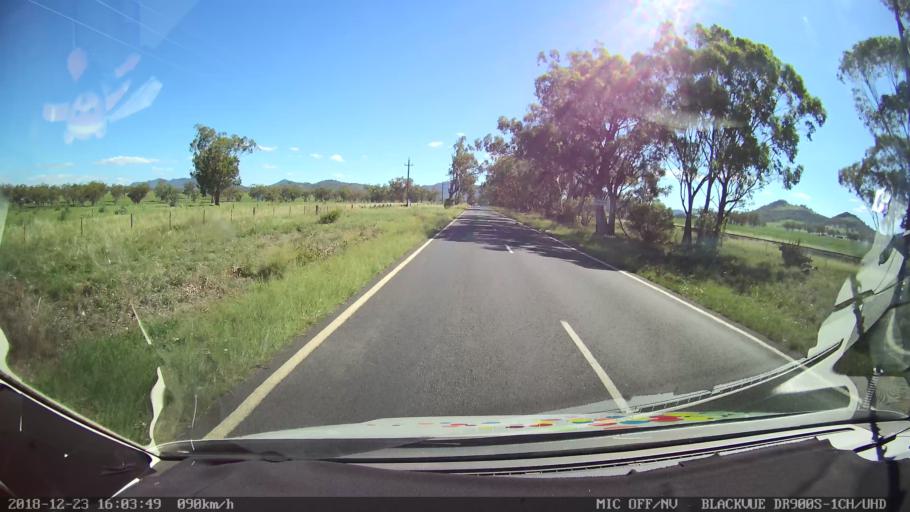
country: AU
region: New South Wales
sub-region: Tamworth Municipality
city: Phillip
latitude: -31.2479
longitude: 150.7975
